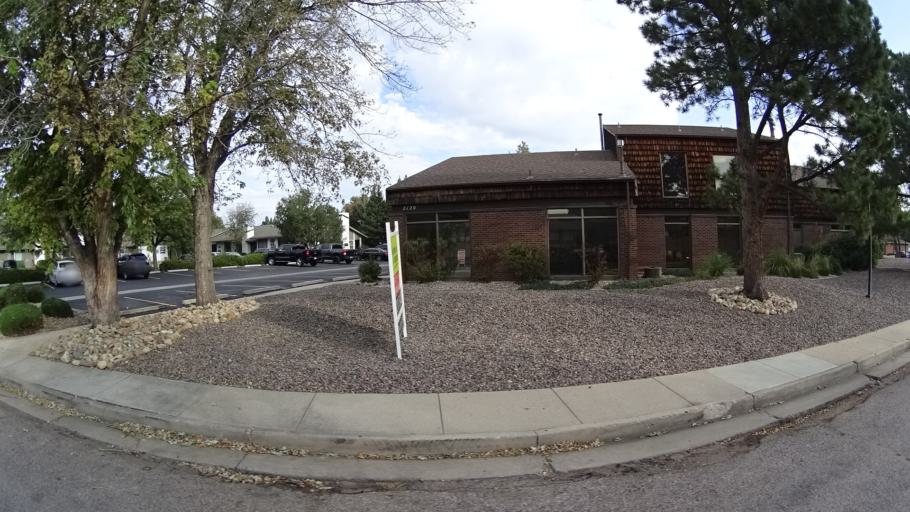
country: US
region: Colorado
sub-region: El Paso County
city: Cimarron Hills
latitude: 38.8629
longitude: -104.7555
